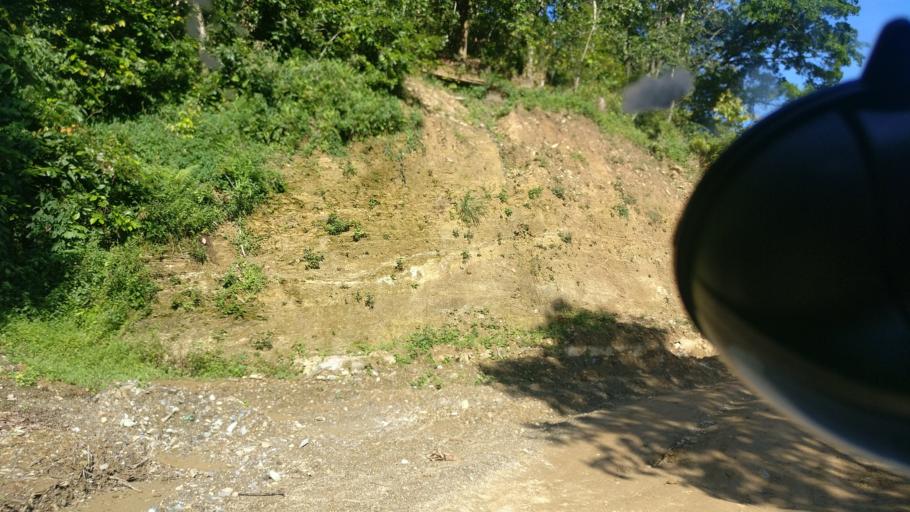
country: NP
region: Western Region
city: Baglung
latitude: 28.1427
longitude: 83.6590
